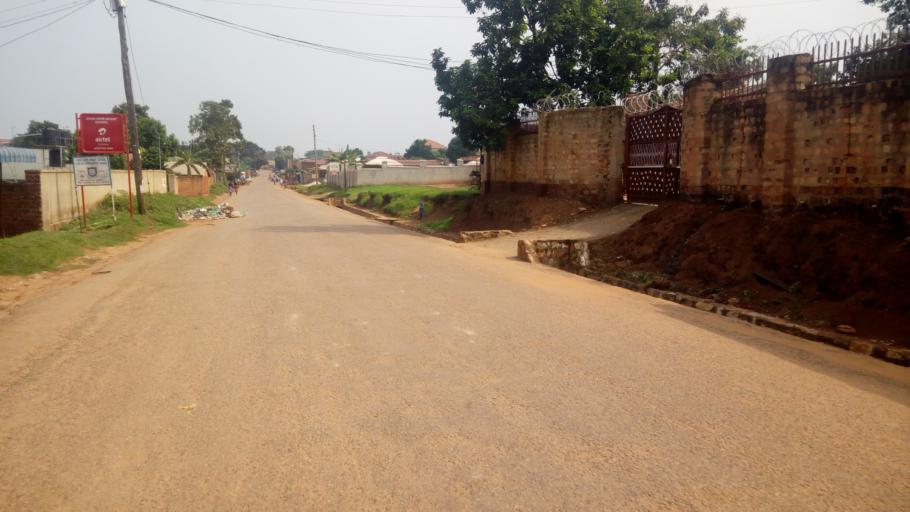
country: UG
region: Central Region
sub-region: Wakiso District
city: Kireka
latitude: 0.3062
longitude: 32.6518
